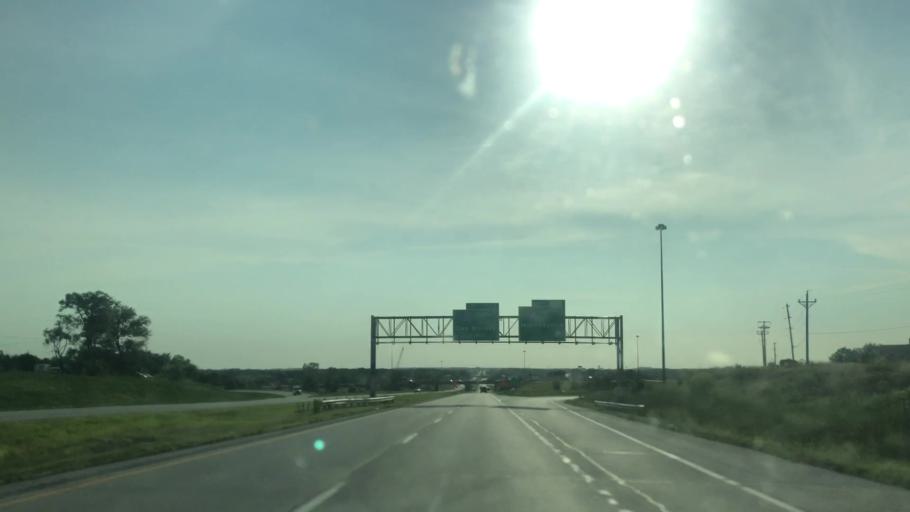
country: US
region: Iowa
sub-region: Story County
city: Ames
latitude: 42.0084
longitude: -93.5640
